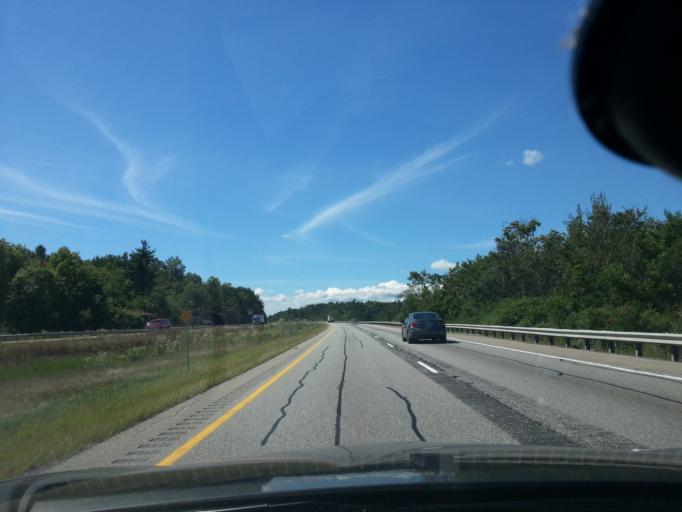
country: US
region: New York
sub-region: Jefferson County
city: Alexandria Bay
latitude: 44.3788
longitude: -76.0264
